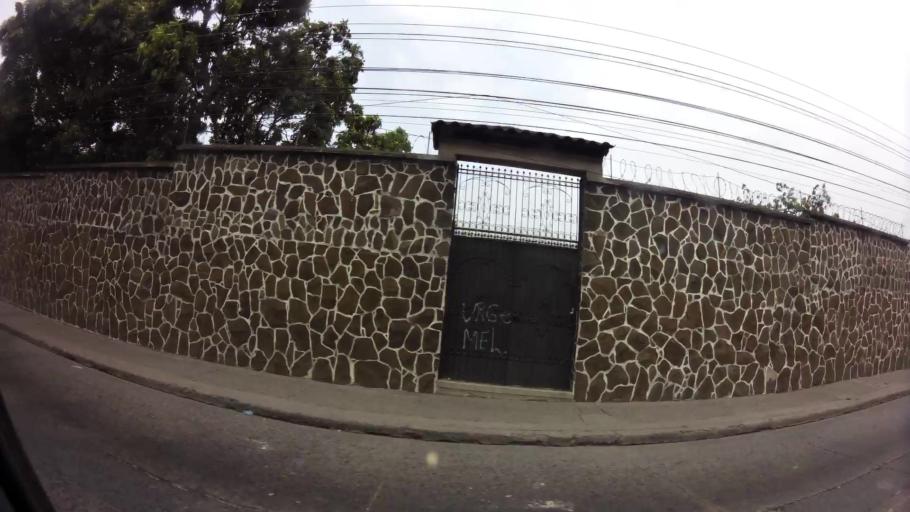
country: HN
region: Francisco Morazan
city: Tegucigalpa
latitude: 14.0814
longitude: -87.2093
